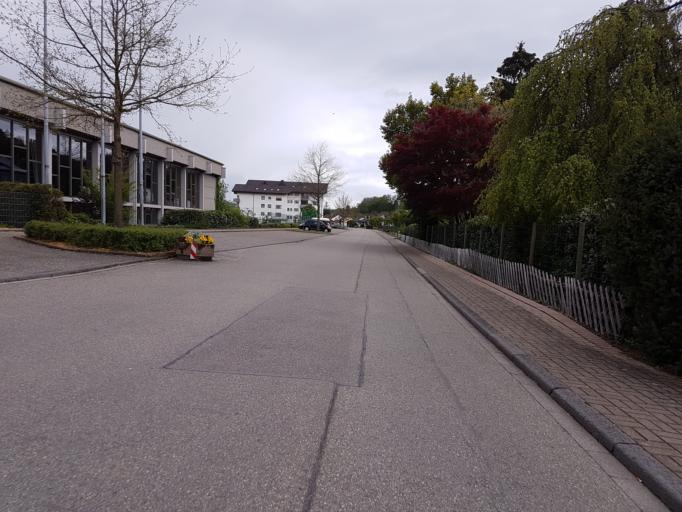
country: DE
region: Baden-Wuerttemberg
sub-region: Freiburg Region
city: Wutoschingen
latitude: 47.6598
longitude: 8.3629
